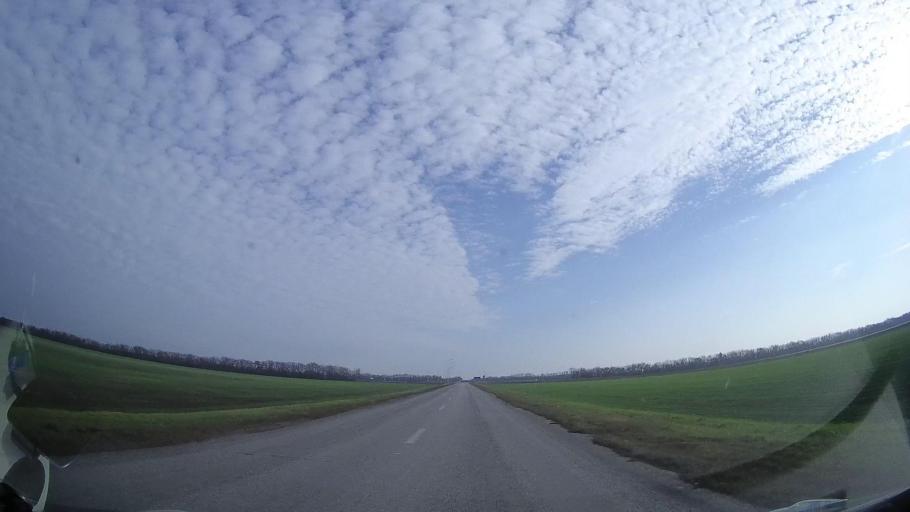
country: RU
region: Rostov
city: Tselina
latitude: 46.5269
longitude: 41.0758
